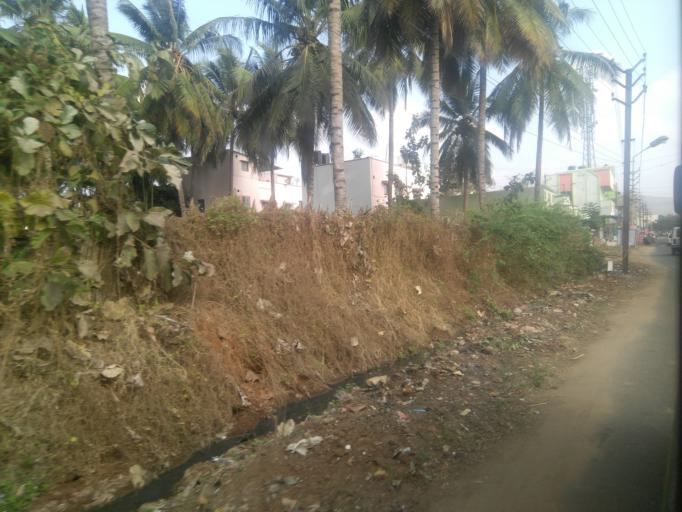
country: IN
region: Tamil Nadu
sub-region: Coimbatore
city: Perur
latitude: 11.0398
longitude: 76.8923
